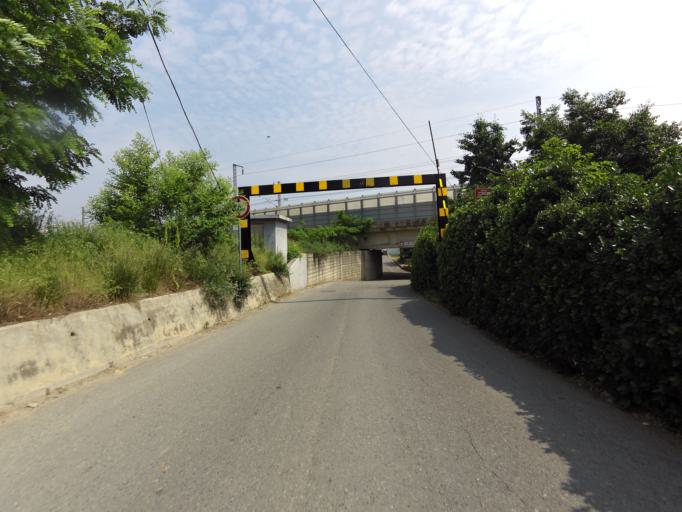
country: KR
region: Gyeongsangbuk-do
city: Gyeongsan-si
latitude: 35.8498
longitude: 128.7078
